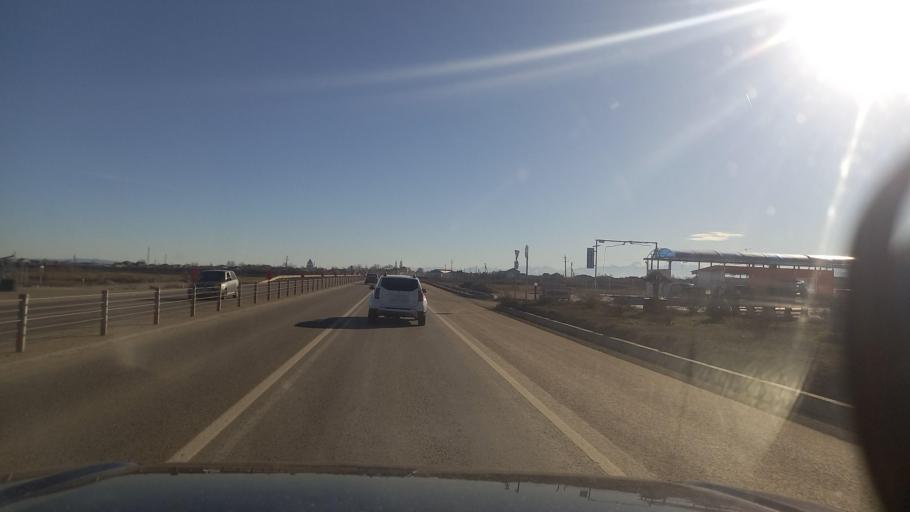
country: RU
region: Kabardino-Balkariya
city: Staryy Cherek
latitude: 43.4731
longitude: 43.8304
